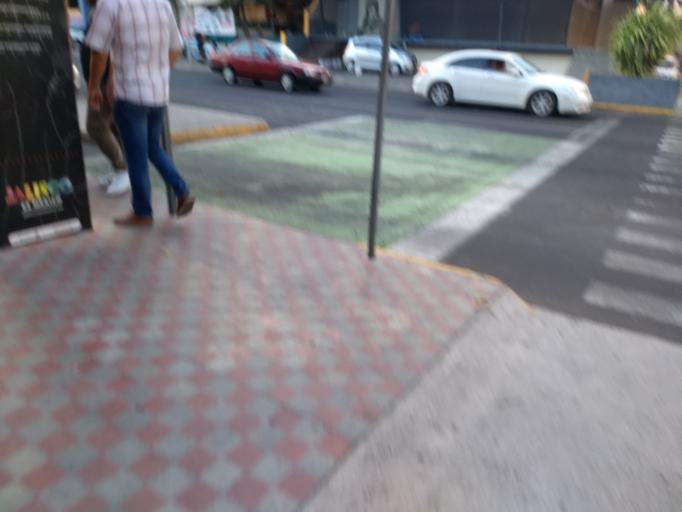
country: MX
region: Jalisco
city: Guadalajara
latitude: 20.6731
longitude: -103.3814
